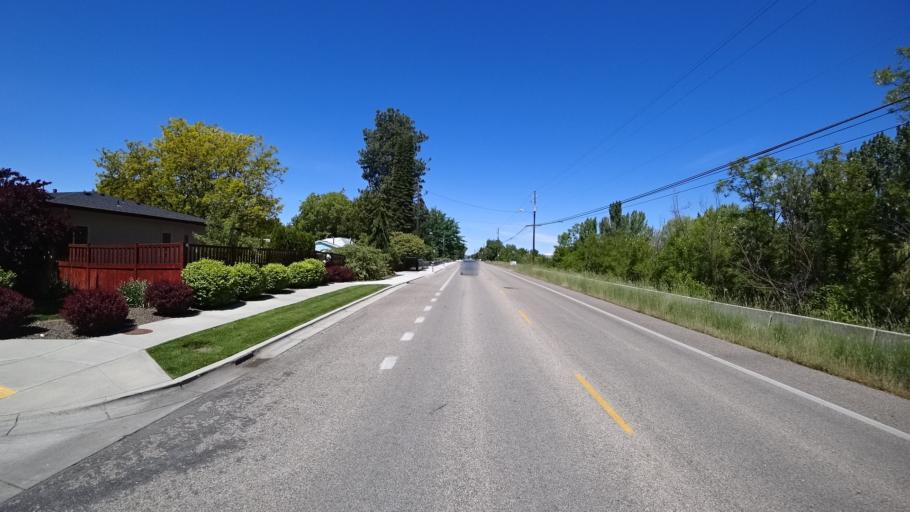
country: US
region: Idaho
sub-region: Ada County
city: Boise
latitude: 43.5682
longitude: -116.1492
